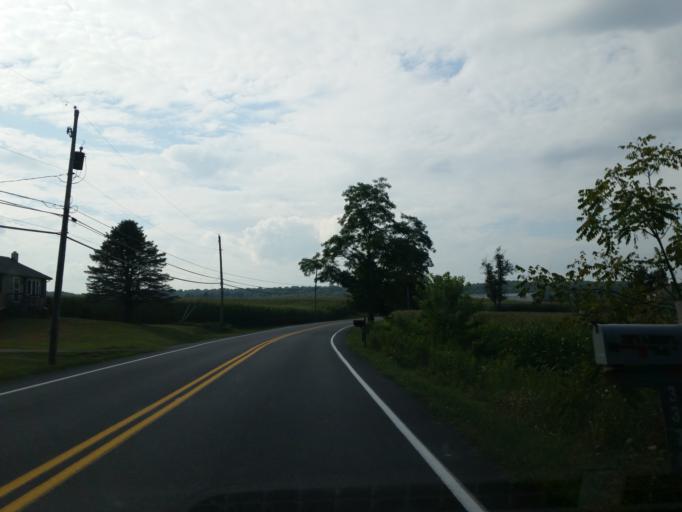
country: US
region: Pennsylvania
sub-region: Lancaster County
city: Mount Joy
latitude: 40.2084
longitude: -76.5038
